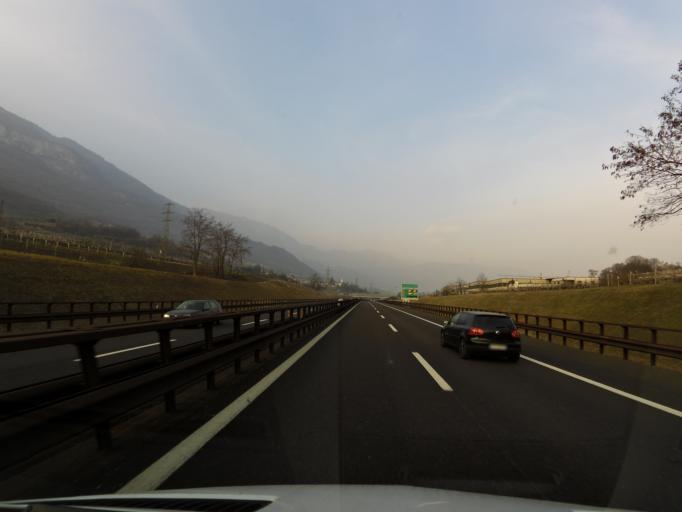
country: IT
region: Trentino-Alto Adige
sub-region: Provincia di Trento
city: Isera
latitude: 45.8767
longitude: 11.0086
